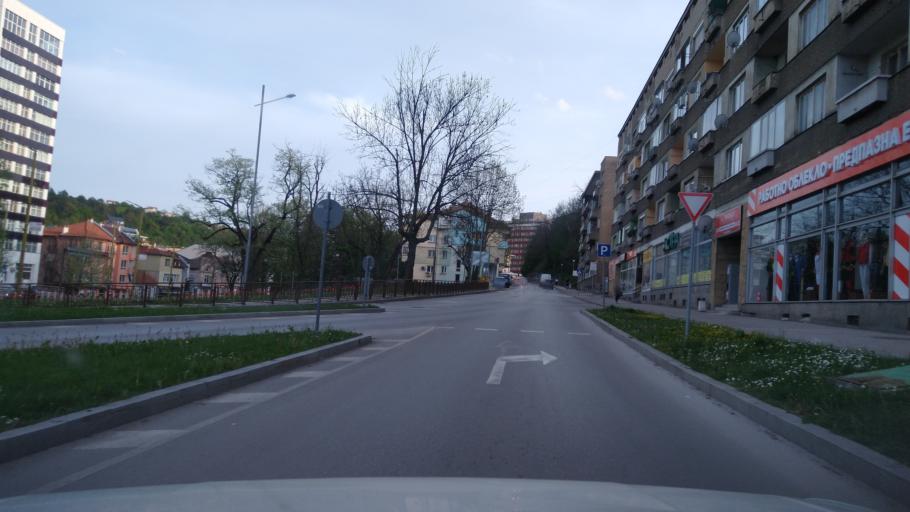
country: BG
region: Gabrovo
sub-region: Obshtina Gabrovo
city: Gabrovo
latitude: 42.8773
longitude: 25.3166
